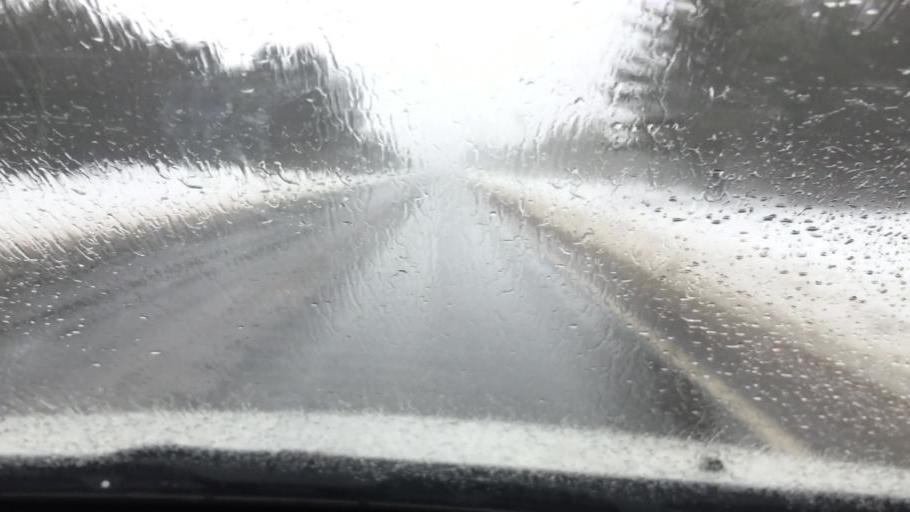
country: US
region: Michigan
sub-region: Antrim County
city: Mancelona
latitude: 44.9351
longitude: -85.0508
